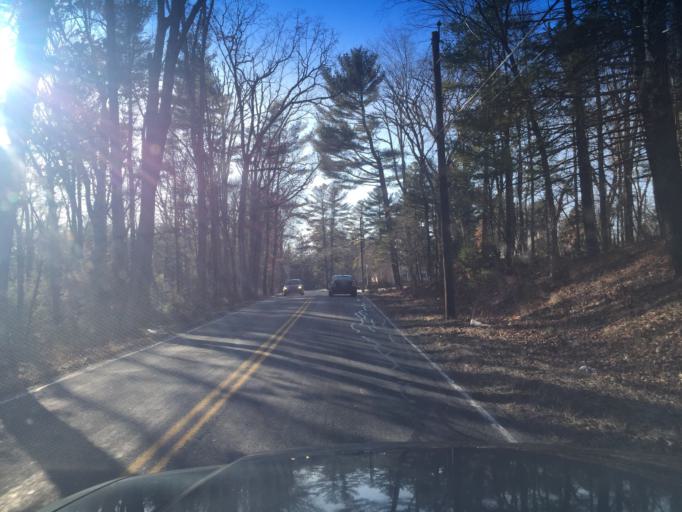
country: US
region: Massachusetts
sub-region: Norfolk County
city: Bellingham
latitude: 42.0893
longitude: -71.5058
